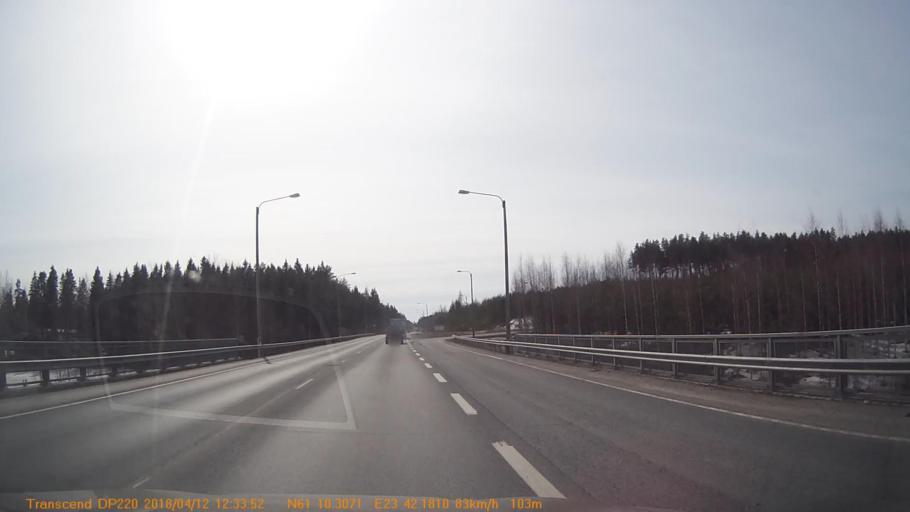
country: FI
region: Pirkanmaa
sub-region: Etelae-Pirkanmaa
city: Kylmaekoski
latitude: 61.1714
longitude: 23.7027
